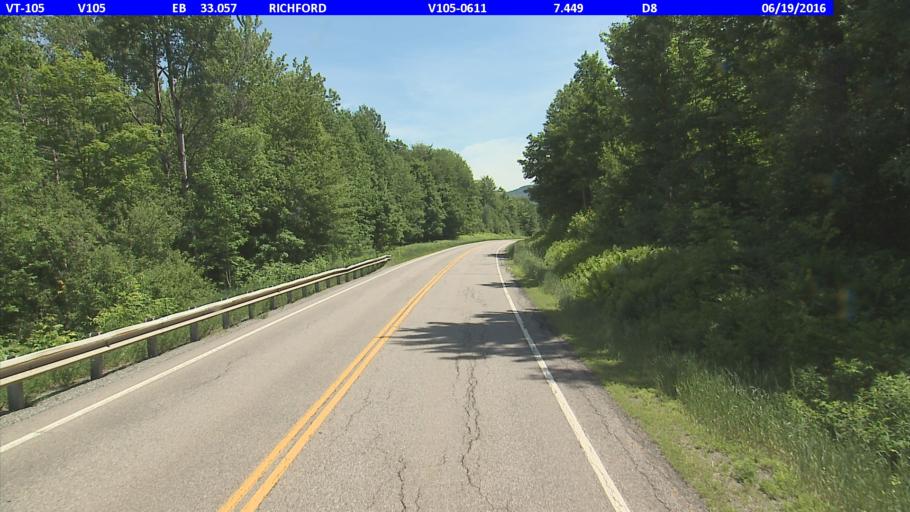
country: US
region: Vermont
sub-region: Franklin County
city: Richford
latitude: 45.0020
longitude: -72.5752
